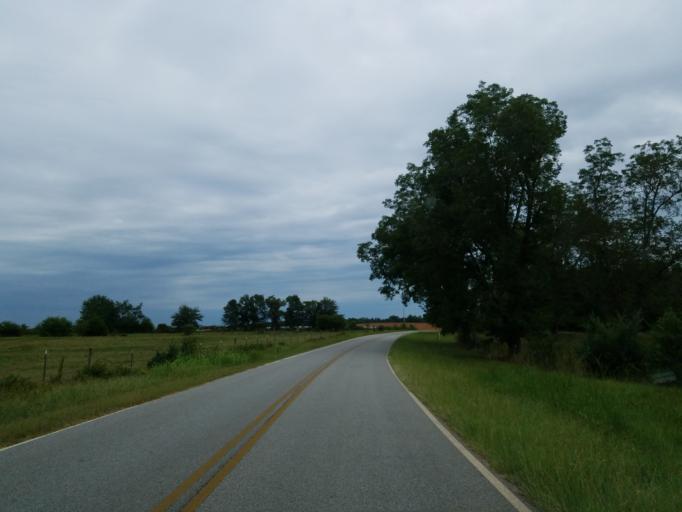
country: US
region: Georgia
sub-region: Lamar County
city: Barnesville
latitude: 33.0087
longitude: -84.0796
